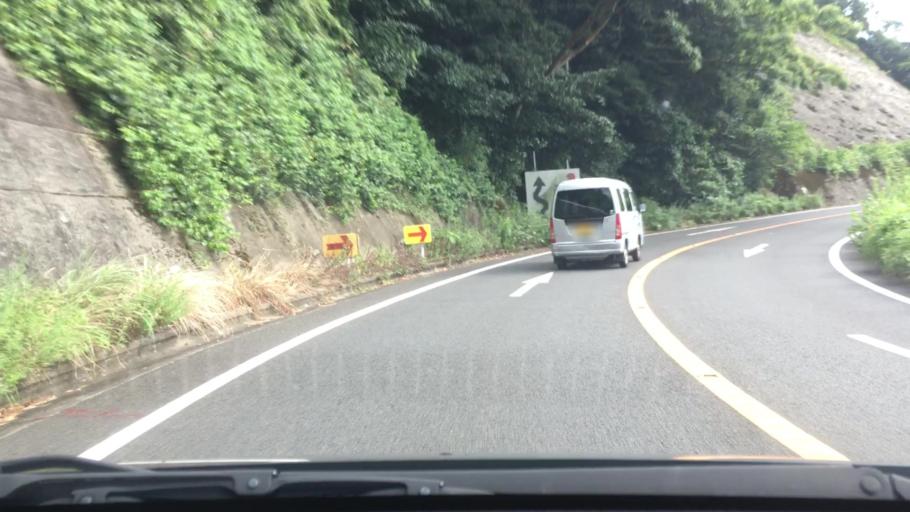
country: JP
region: Nagasaki
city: Togitsu
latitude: 32.8390
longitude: 129.7055
